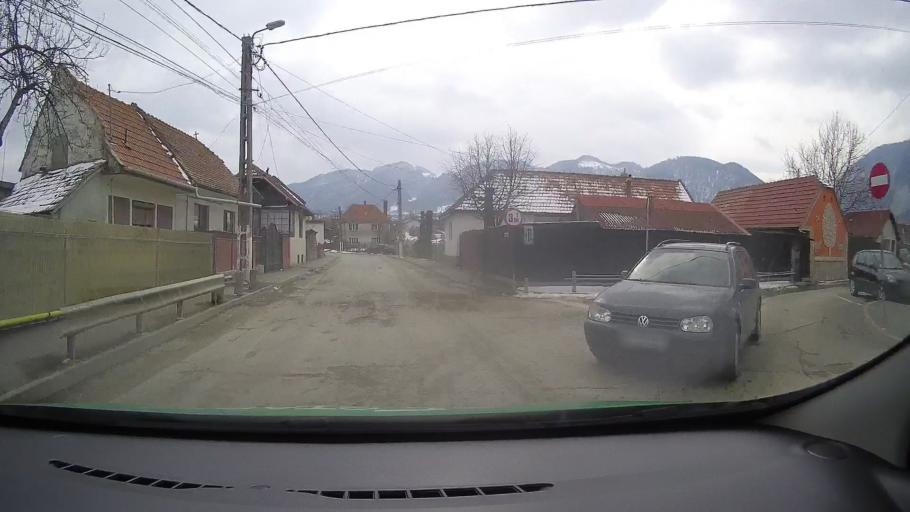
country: RO
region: Brasov
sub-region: Comuna Zarnesti
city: Zarnesti
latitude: 45.5582
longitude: 25.3244
